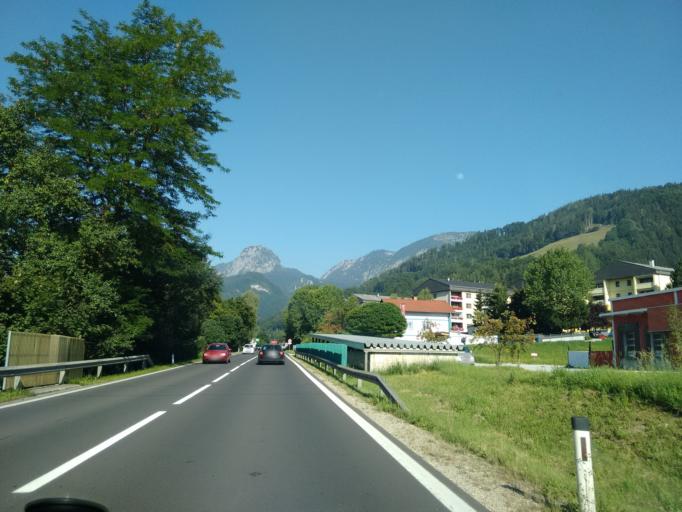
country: AT
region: Styria
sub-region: Politischer Bezirk Liezen
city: Liezen
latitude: 47.5678
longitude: 14.2311
